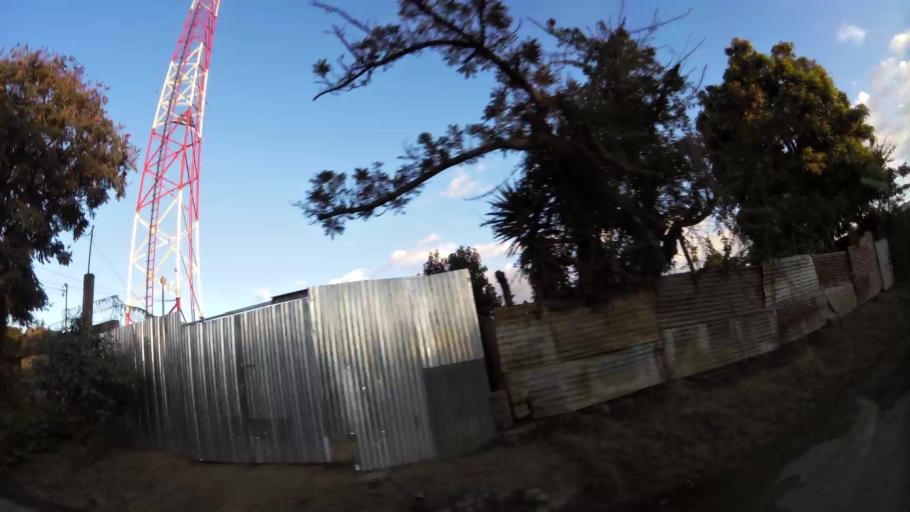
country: GT
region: Guatemala
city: Petapa
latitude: 14.5022
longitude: -90.5774
